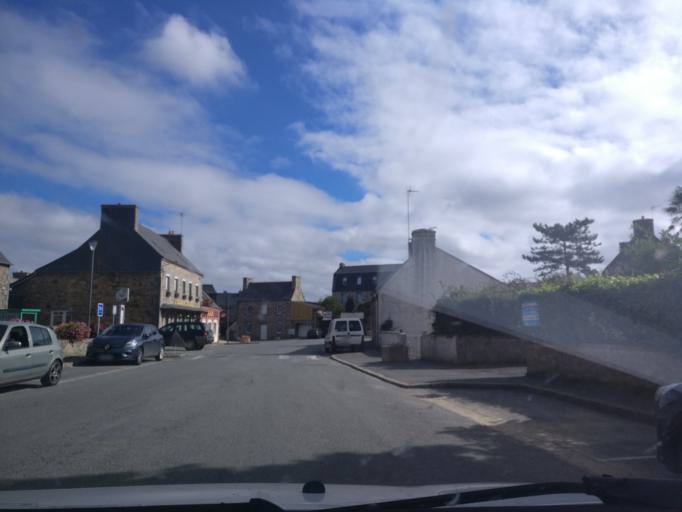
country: FR
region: Brittany
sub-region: Departement des Cotes-d'Armor
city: Rospez
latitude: 48.7291
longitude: -3.3853
